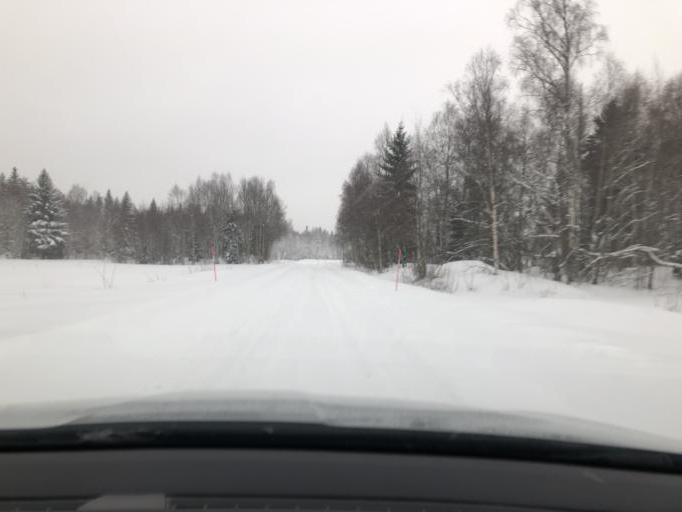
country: SE
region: Vaesterbotten
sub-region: Umea Kommun
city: Saevar
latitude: 63.9434
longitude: 20.7097
